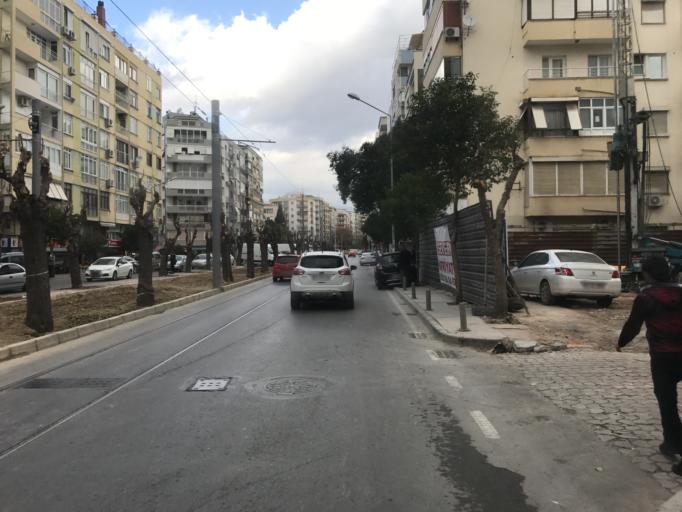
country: TR
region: Izmir
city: Izmir
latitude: 38.4322
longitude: 27.1435
